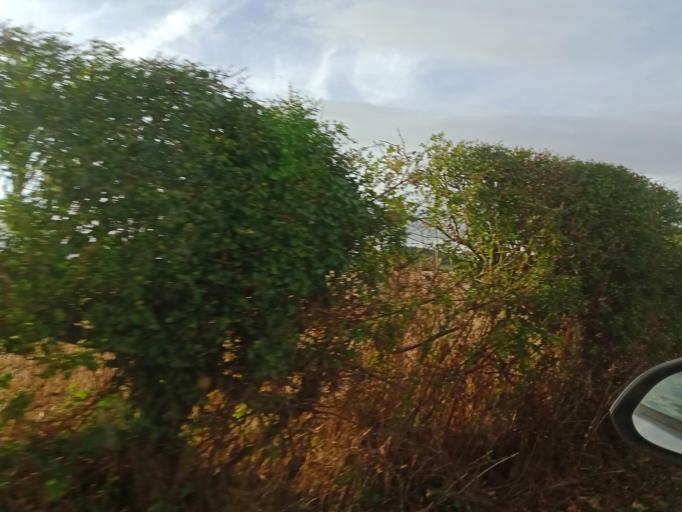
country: IE
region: Leinster
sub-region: Laois
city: Stradbally
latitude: 53.0013
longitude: -7.2124
